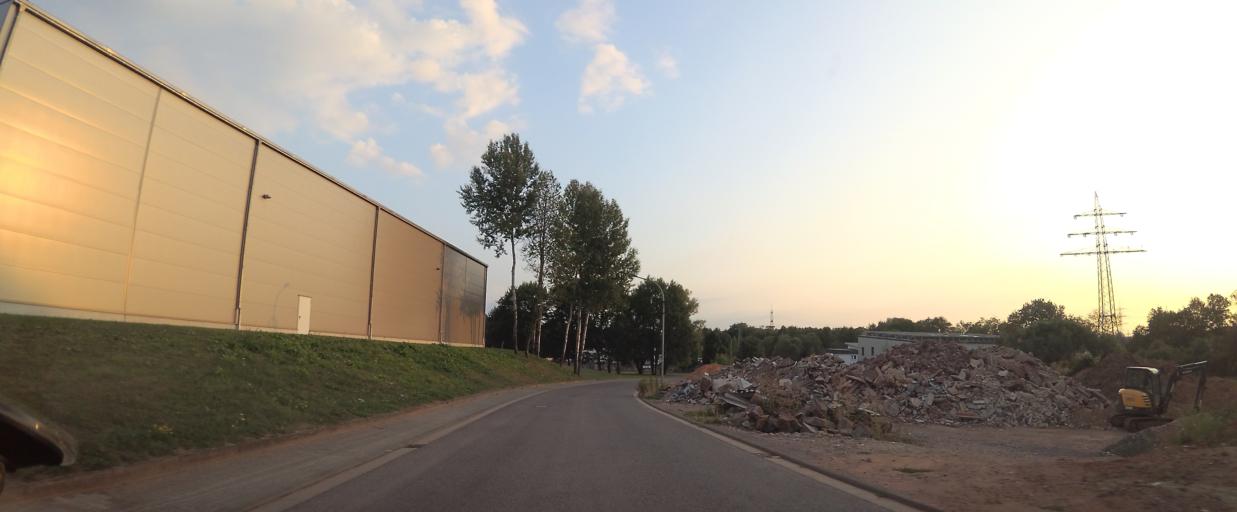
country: DE
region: Saarland
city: Wadern
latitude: 49.5266
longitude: 6.8986
